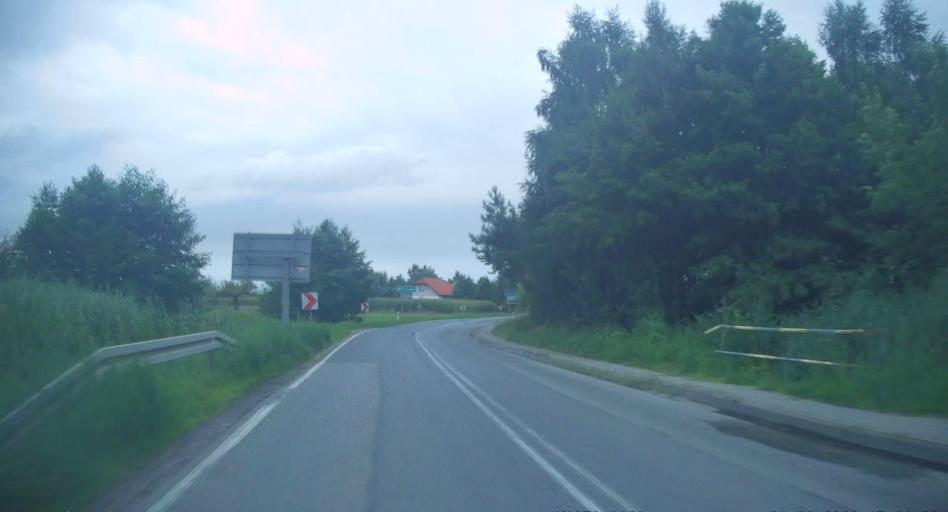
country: PL
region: Lesser Poland Voivodeship
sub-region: Powiat tarnowski
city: Wierzchoslawice
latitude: 50.0105
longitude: 20.8672
